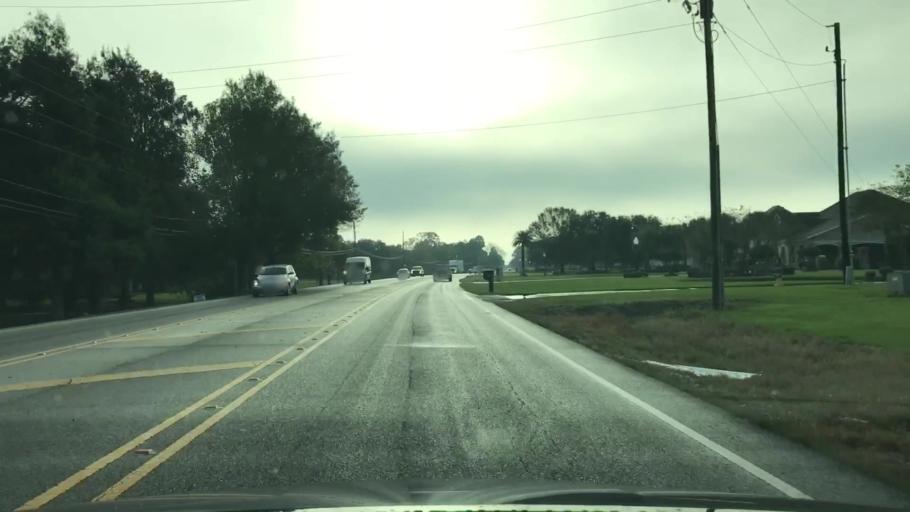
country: US
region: Louisiana
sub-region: Terrebonne Parish
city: Bayou Cane
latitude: 29.6135
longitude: -90.7836
